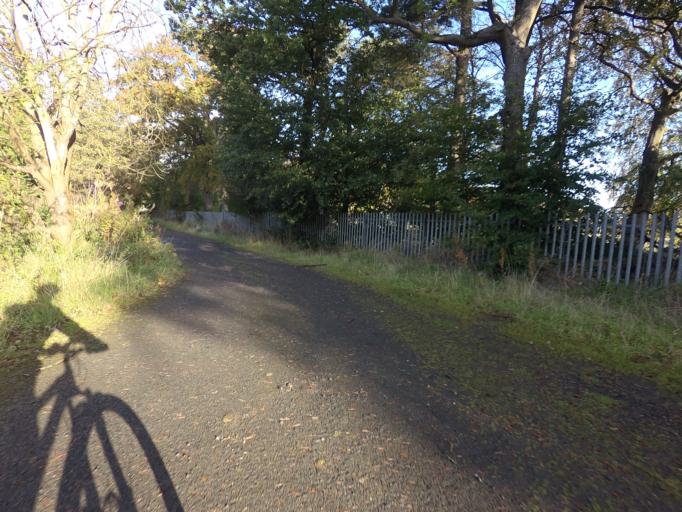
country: GB
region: Scotland
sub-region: West Lothian
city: West Calder
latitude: 55.8605
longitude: -3.5430
